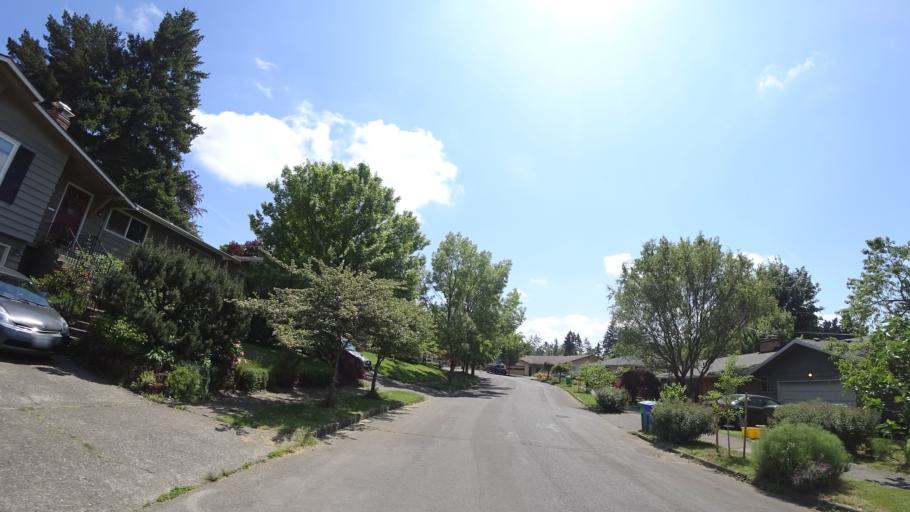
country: US
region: Oregon
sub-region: Multnomah County
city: Portland
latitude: 45.4720
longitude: -122.6933
